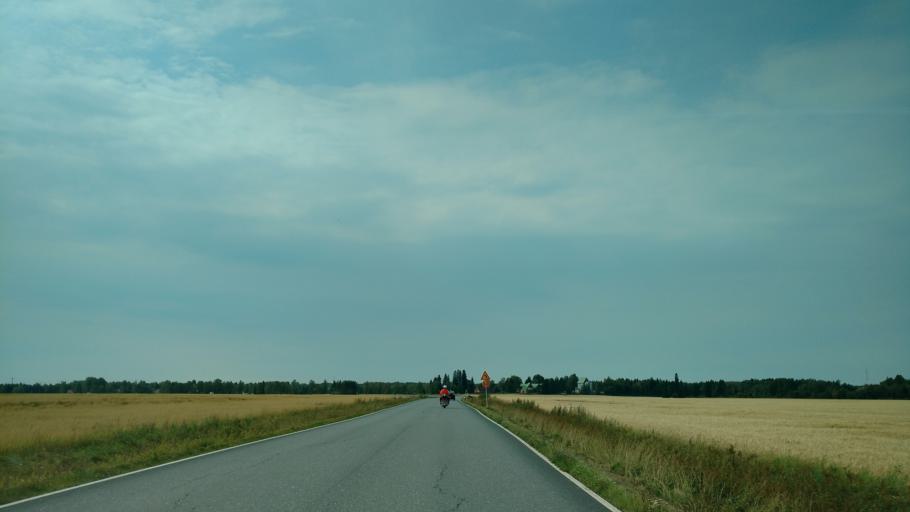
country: FI
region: Varsinais-Suomi
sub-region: Loimaa
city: Koski Tl
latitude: 60.6719
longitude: 23.1578
